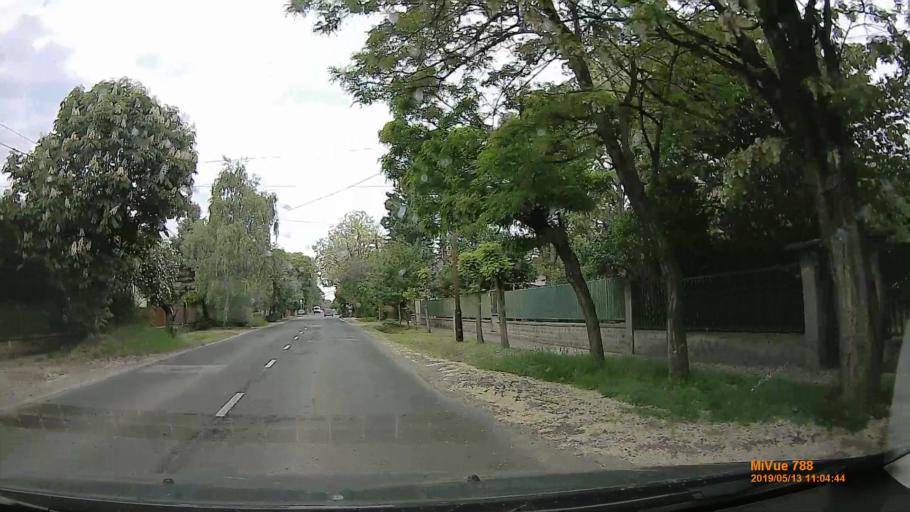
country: HU
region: Budapest
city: Budapest XXIII. keruelet
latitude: 47.3976
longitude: 19.0908
